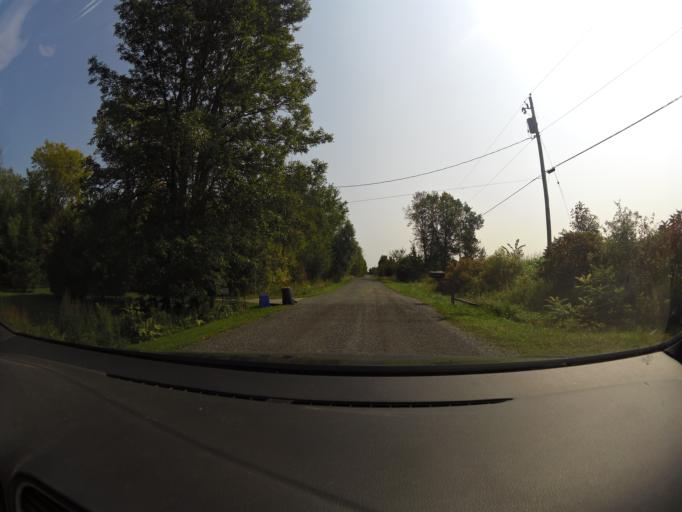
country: CA
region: Ontario
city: Arnprior
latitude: 45.4494
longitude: -76.1678
